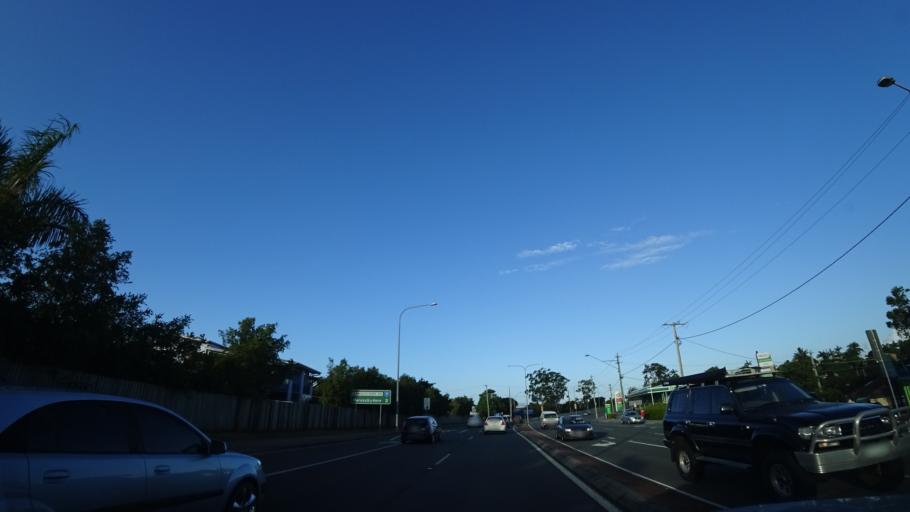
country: AU
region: Queensland
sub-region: Sunshine Coast
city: Buderim
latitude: -26.6558
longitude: 153.0724
